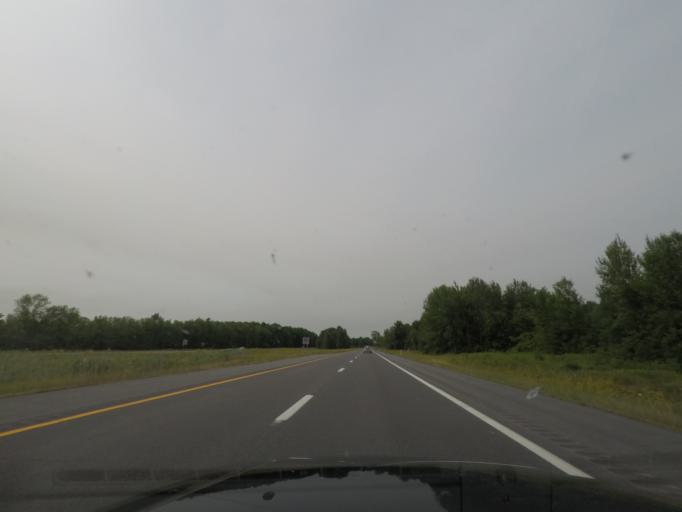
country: US
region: New York
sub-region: Clinton County
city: Cumberland Head
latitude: 44.8465
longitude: -73.4473
